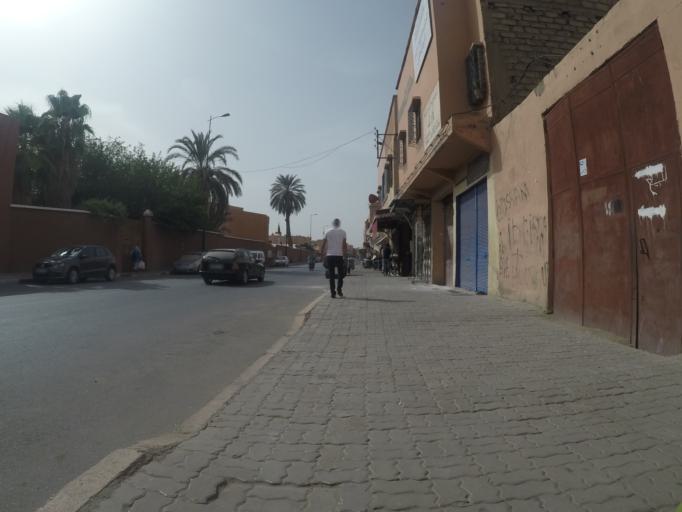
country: MA
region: Marrakech-Tensift-Al Haouz
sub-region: Marrakech
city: Marrakesh
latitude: 31.6255
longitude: -7.9772
